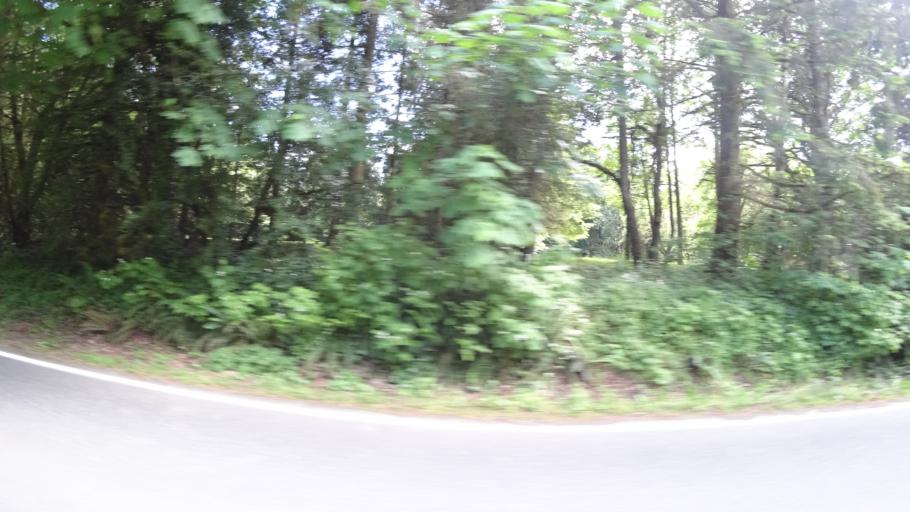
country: US
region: Oregon
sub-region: Washington County
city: Oak Hills
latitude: 45.5886
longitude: -122.8070
